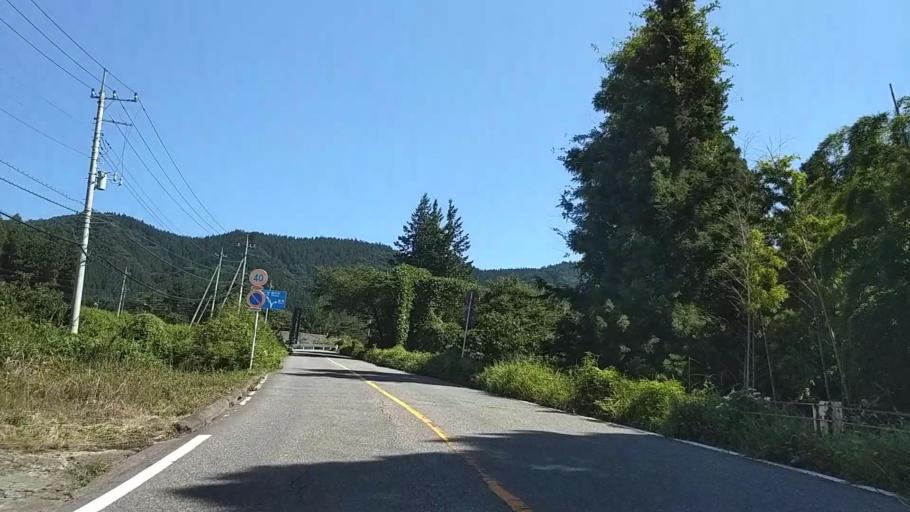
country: JP
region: Gunma
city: Annaka
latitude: 36.3535
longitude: 138.7159
